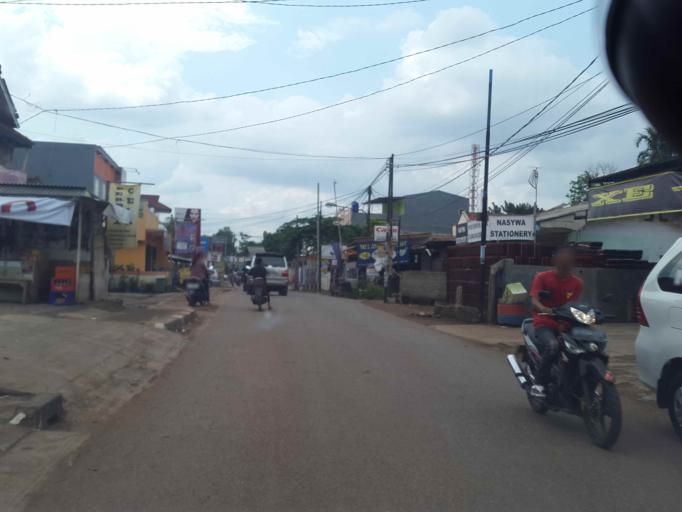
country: ID
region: West Java
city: Cileungsir
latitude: -6.3626
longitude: 106.9220
